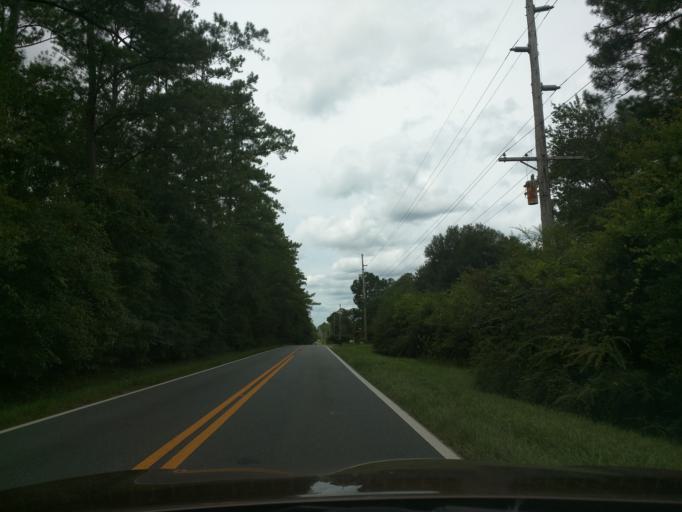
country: US
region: Florida
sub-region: Leon County
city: Tallahassee
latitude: 30.5364
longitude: -84.1374
